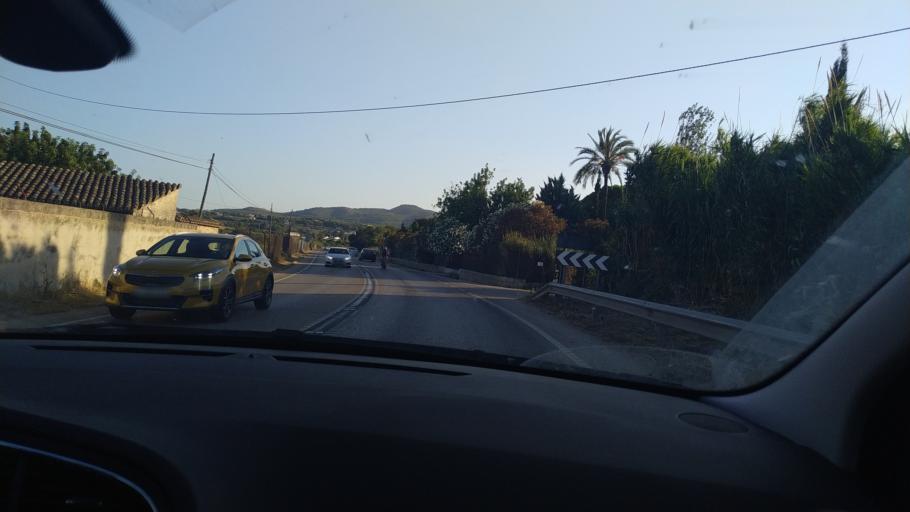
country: ES
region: Valencia
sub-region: Provincia de Alicante
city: Javea
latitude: 38.7794
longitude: 0.1486
